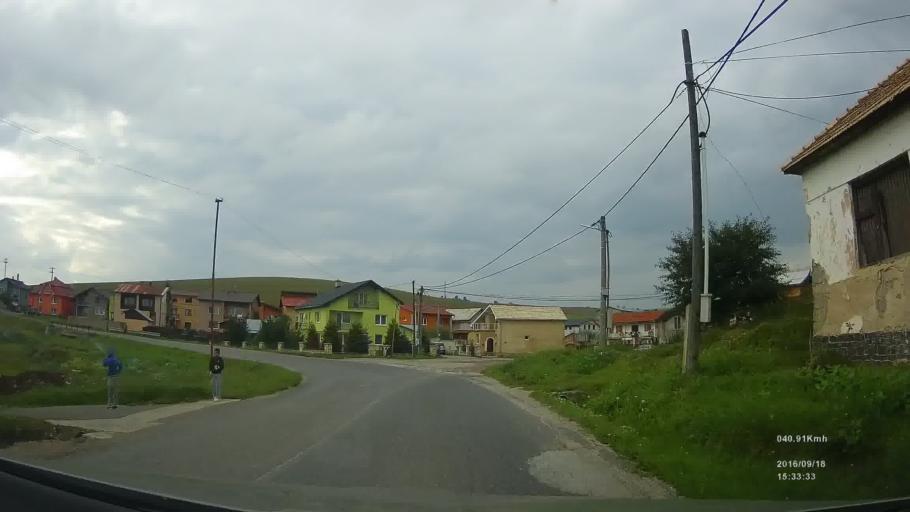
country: SK
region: Kosicky
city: Spisska Nova Ves
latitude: 49.0006
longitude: 20.4597
